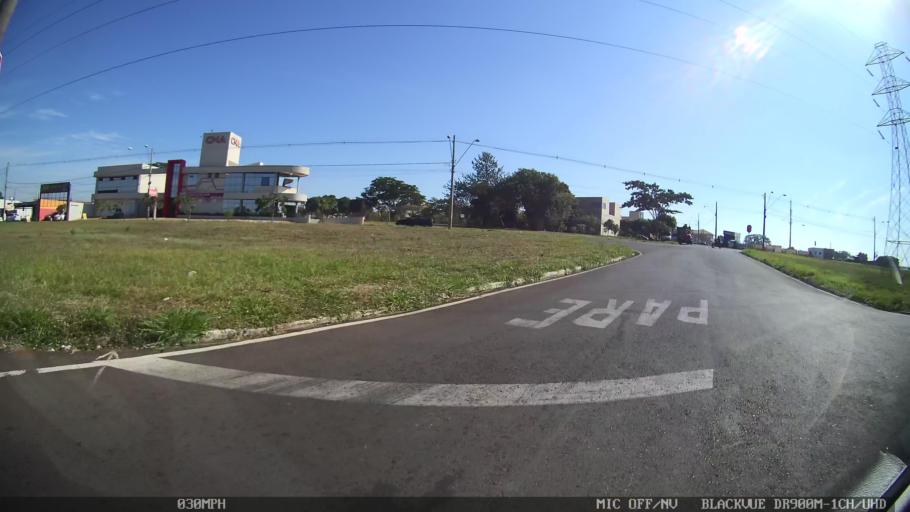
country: BR
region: Sao Paulo
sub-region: Sao Jose Do Rio Preto
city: Sao Jose do Rio Preto
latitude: -20.7700
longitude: -49.3898
